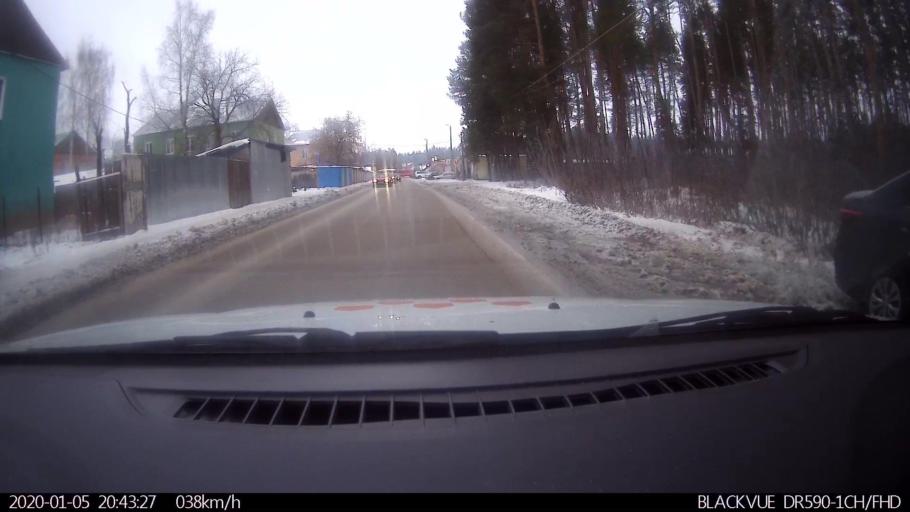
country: RU
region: Nizjnij Novgorod
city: Lukino
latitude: 56.3905
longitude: 43.7394
